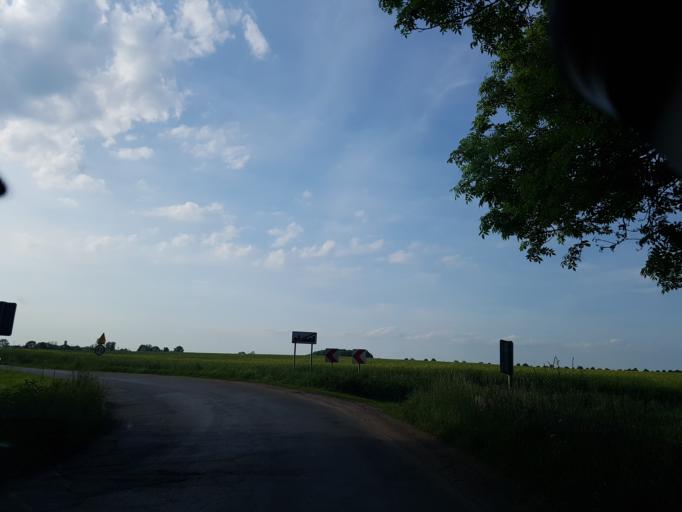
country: PL
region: Lower Silesian Voivodeship
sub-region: Powiat wroclawski
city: Zorawina
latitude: 50.9100
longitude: 17.0039
